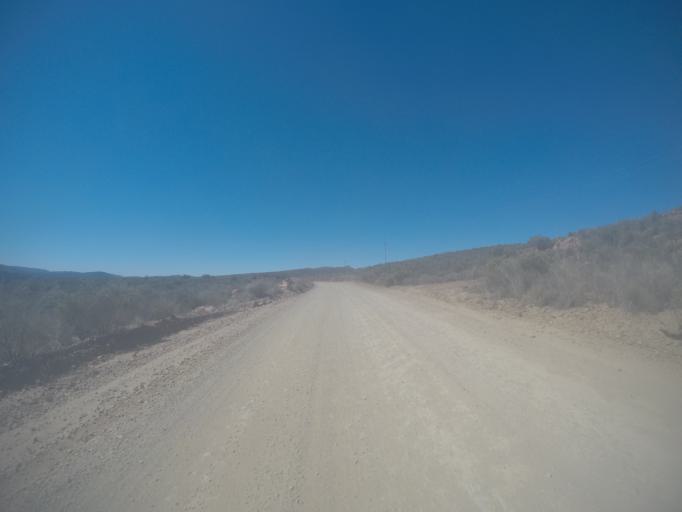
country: ZA
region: Western Cape
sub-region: West Coast District Municipality
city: Clanwilliam
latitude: -32.4978
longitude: 19.2742
